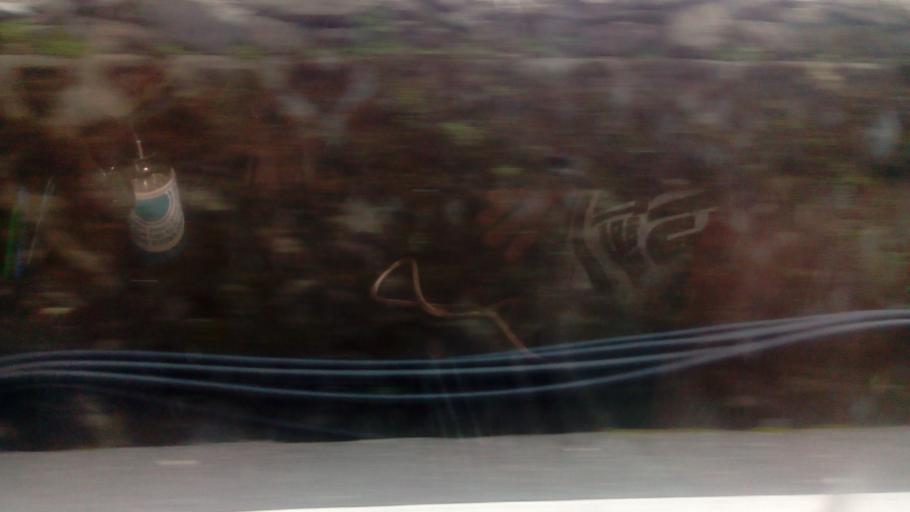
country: TW
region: Taiwan
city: Daxi
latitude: 24.4643
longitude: 121.3965
